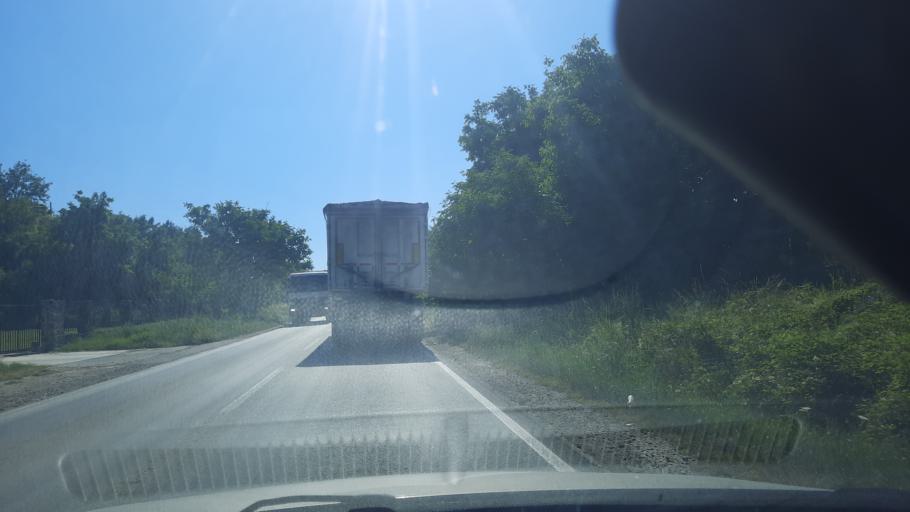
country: RS
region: Autonomna Pokrajina Vojvodina
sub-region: Juznobacki Okrug
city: Novi Sad
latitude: 45.2130
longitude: 19.7978
